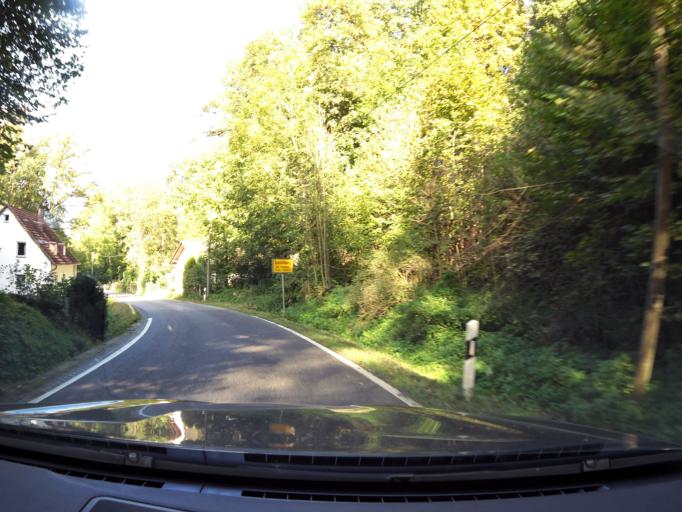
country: DE
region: Bavaria
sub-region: Lower Bavaria
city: Tiefenbach
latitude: 48.5141
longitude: 12.1118
